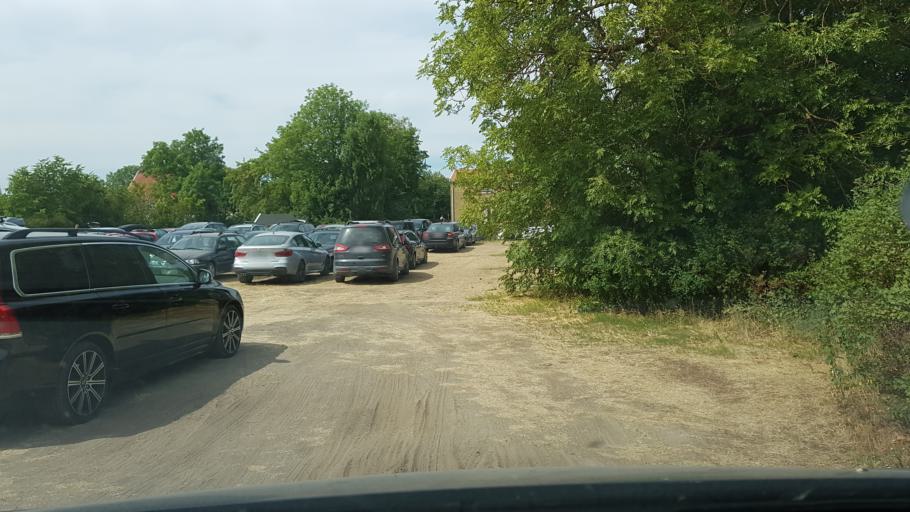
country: SE
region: Gotland
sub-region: Gotland
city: Slite
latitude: 57.7032
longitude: 18.8046
